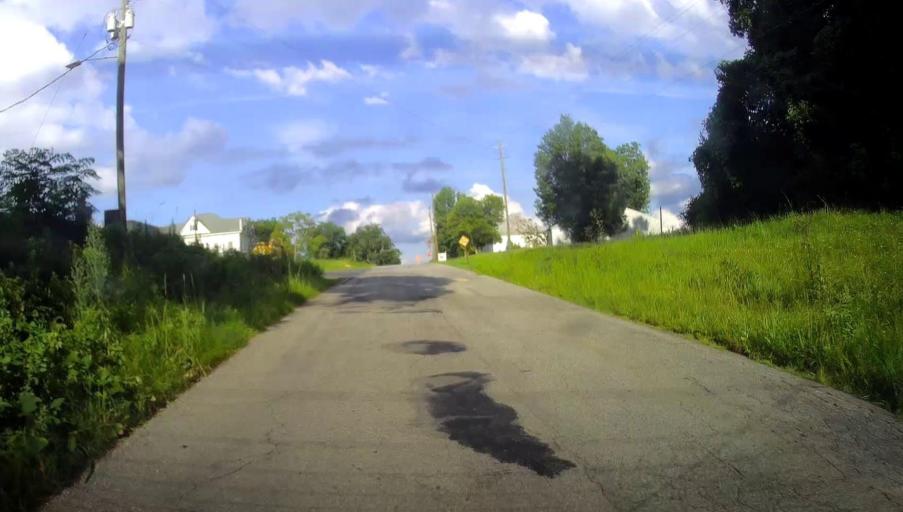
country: US
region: Georgia
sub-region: Crawford County
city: Knoxville
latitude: 32.7240
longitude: -83.9992
